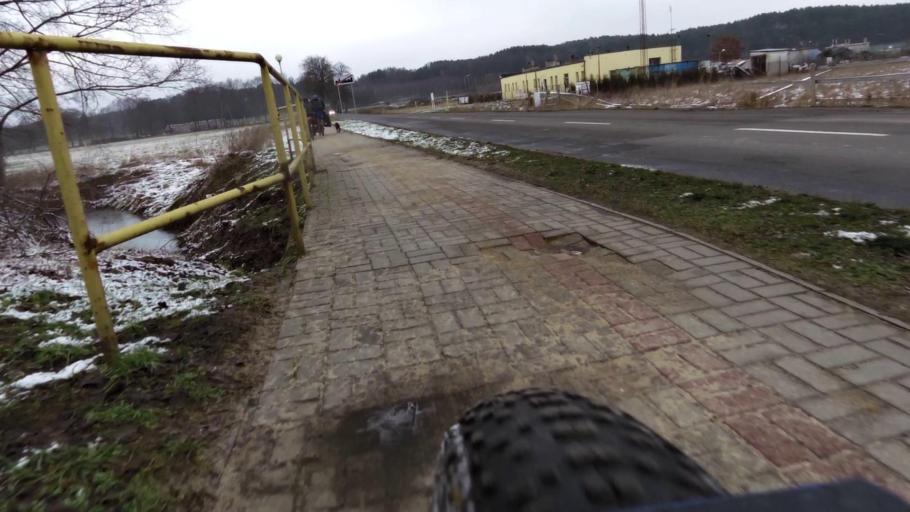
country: PL
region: West Pomeranian Voivodeship
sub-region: Powiat walecki
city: Miroslawiec
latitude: 53.3507
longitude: 16.0863
